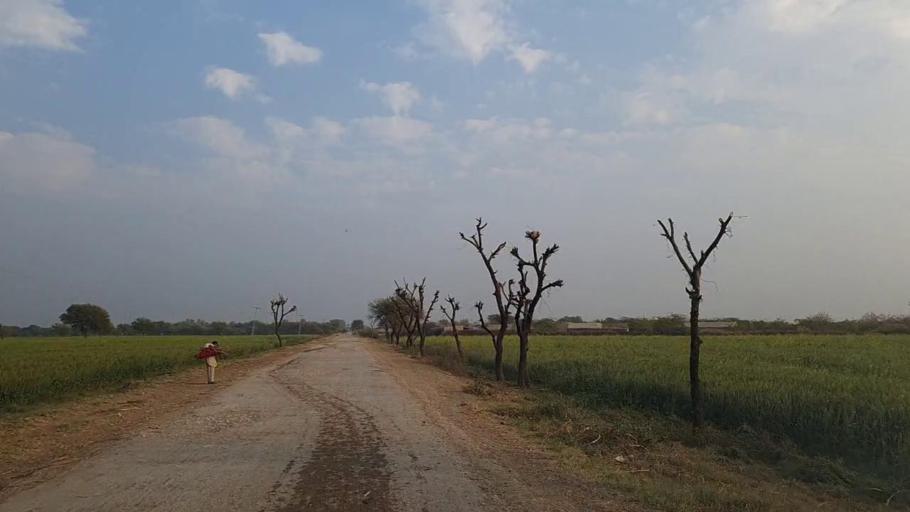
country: PK
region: Sindh
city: Samaro
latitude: 25.2933
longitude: 69.2297
